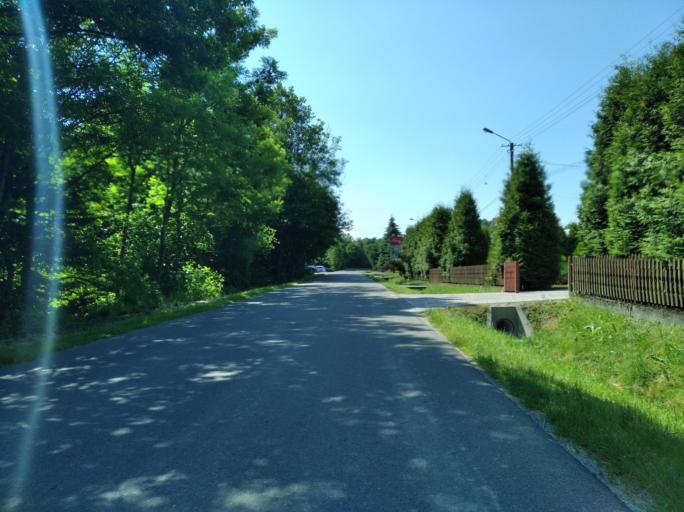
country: PL
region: Subcarpathian Voivodeship
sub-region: Powiat ropczycko-sedziszowski
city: Zagorzyce
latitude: 50.0016
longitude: 21.6533
